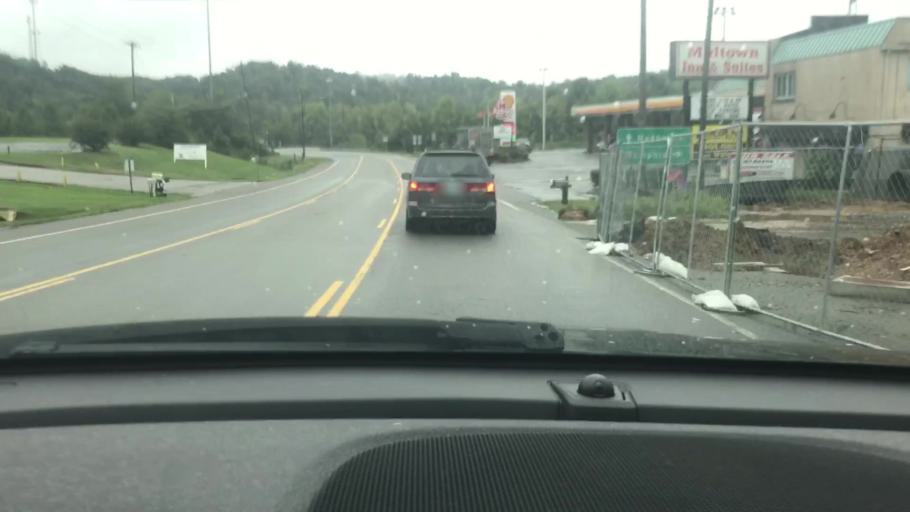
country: US
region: Tennessee
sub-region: Cheatham County
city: Kingston Springs
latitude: 36.0855
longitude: -87.1000
